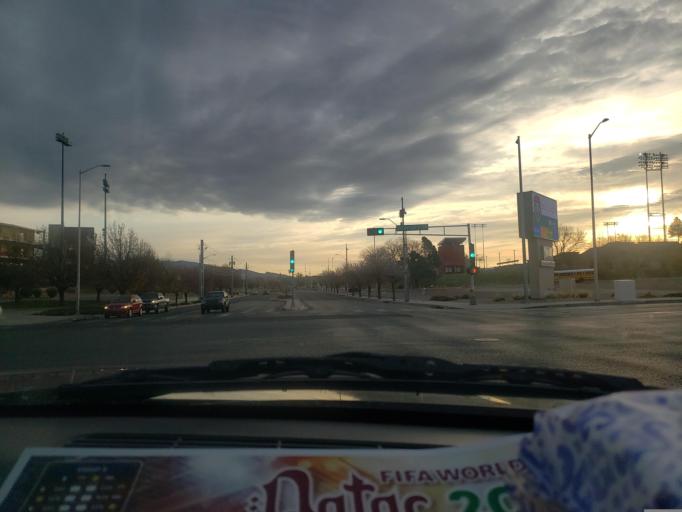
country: US
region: New Mexico
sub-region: Bernalillo County
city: Albuquerque
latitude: 35.0684
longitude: -106.6311
